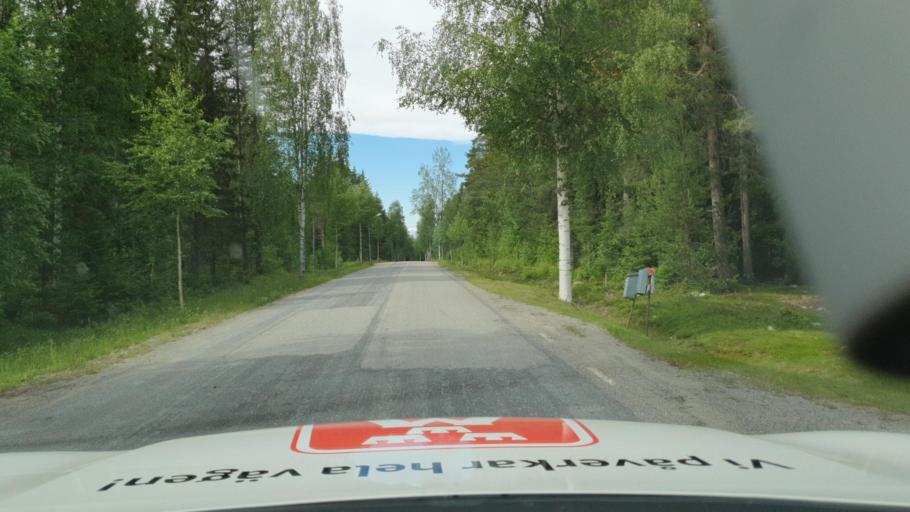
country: SE
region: Vaesterbotten
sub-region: Skelleftea Kommun
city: Burtraesk
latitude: 64.4407
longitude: 20.4920
